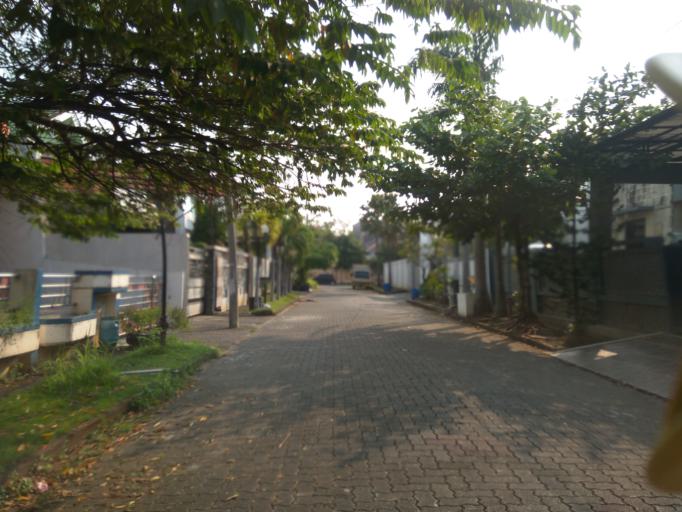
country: ID
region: Central Java
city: Semarang
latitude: -6.9650
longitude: 110.3849
